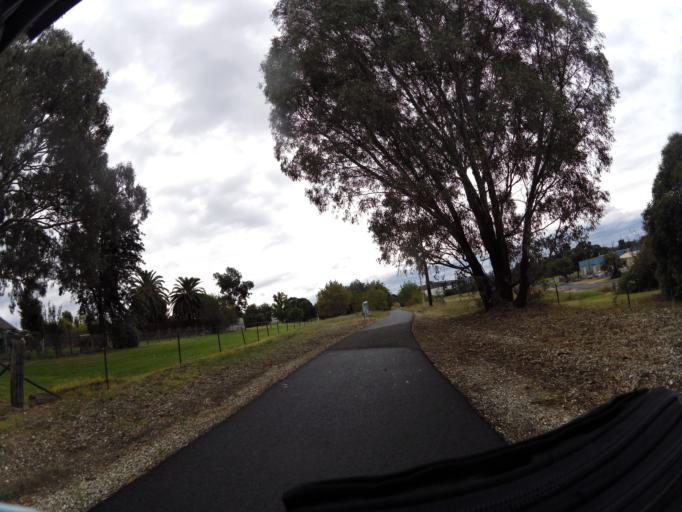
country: AU
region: Victoria
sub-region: Wodonga
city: Wodonga
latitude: -36.1248
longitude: 146.8935
